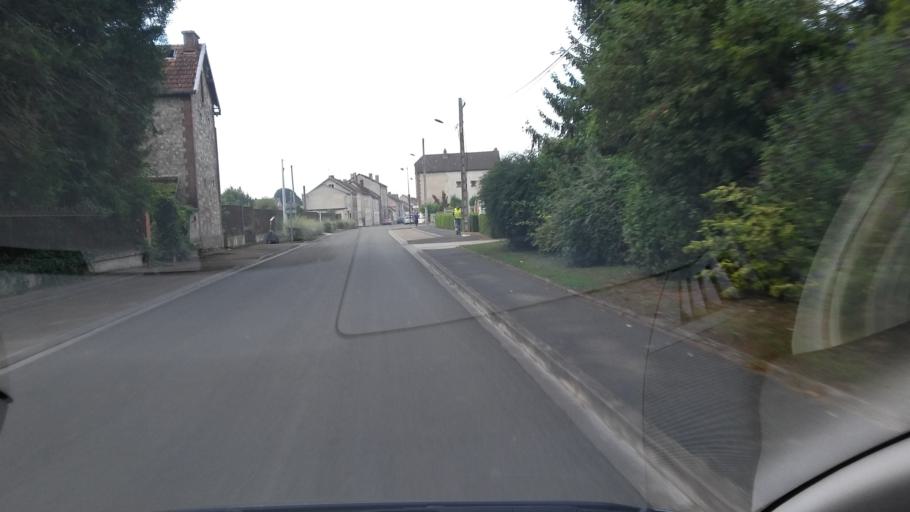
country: FR
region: Champagne-Ardenne
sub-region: Departement de la Marne
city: Fere-Champenoise
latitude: 48.7574
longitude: 3.9953
